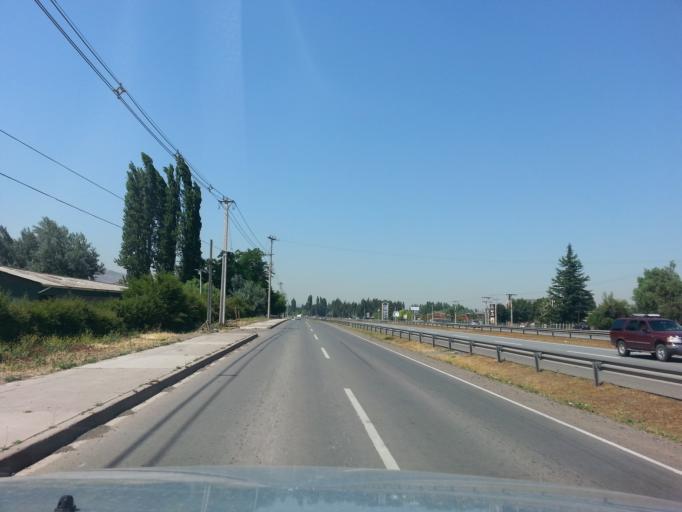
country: CL
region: Santiago Metropolitan
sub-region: Provincia de Chacabuco
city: Chicureo Abajo
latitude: -33.2738
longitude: -70.7013
